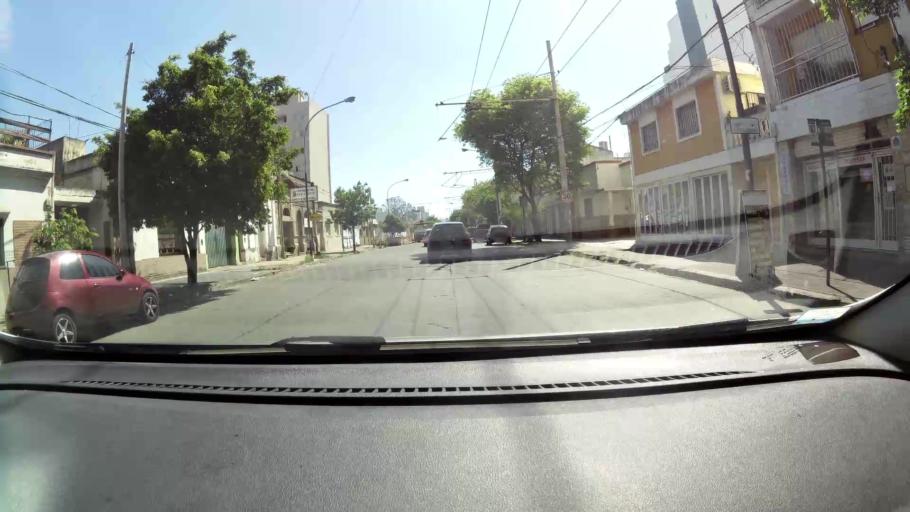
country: AR
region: Cordoba
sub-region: Departamento de Capital
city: Cordoba
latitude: -31.4103
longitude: -64.1663
